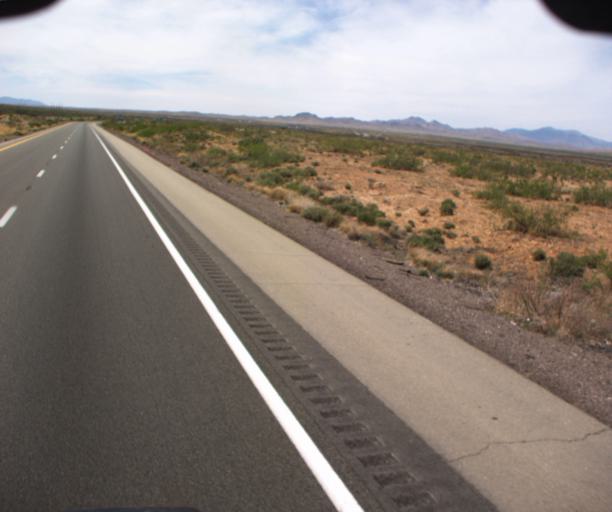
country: US
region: Arizona
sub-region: Cochise County
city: Willcox
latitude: 32.3467
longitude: -109.5960
